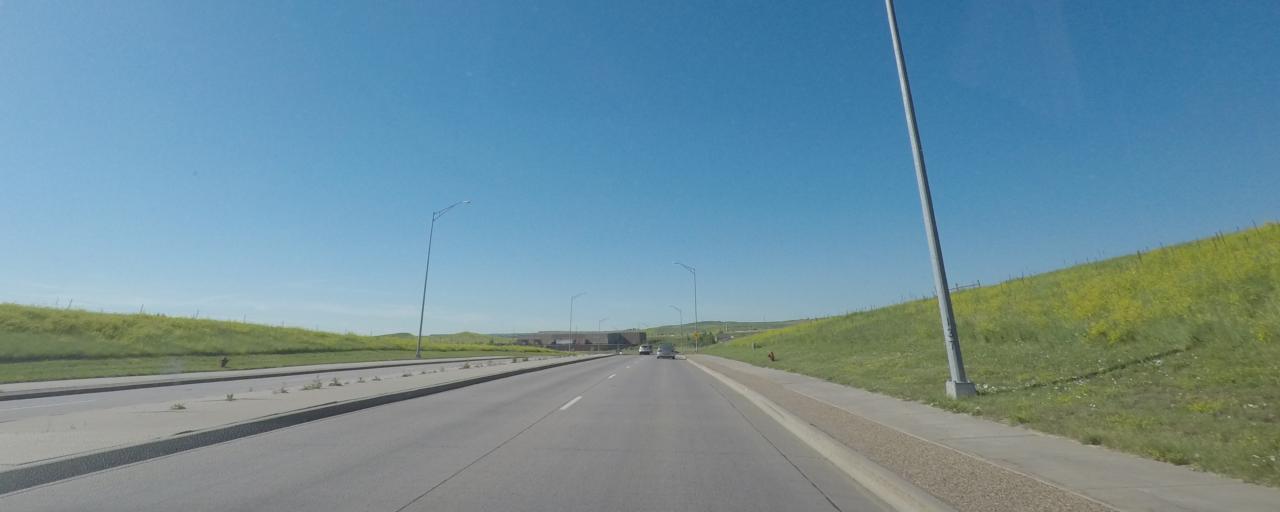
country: US
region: South Dakota
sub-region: Pennington County
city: Rapid City
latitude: 44.0404
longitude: -103.2193
